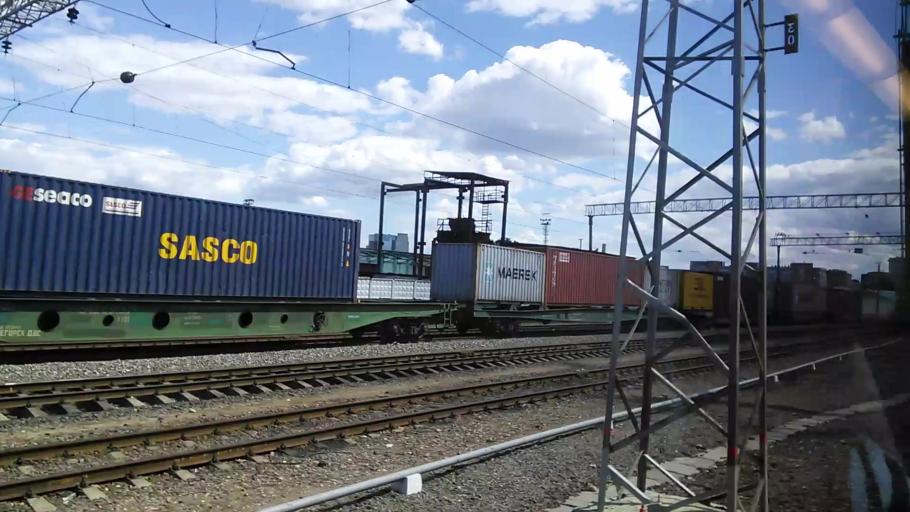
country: RU
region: Moscow
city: Mar'ina Roshcha
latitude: 55.7993
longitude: 37.5887
